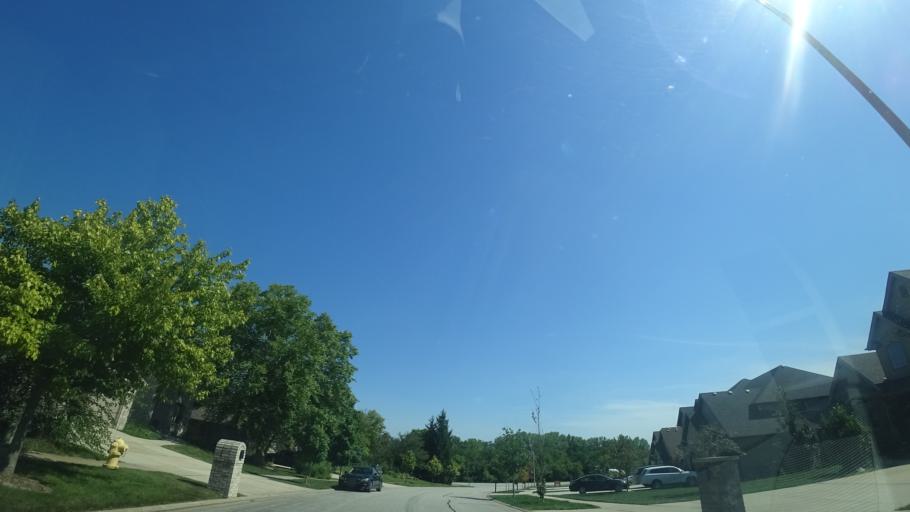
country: US
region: Illinois
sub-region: Will County
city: Mokena
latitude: 41.5702
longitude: -87.8976
